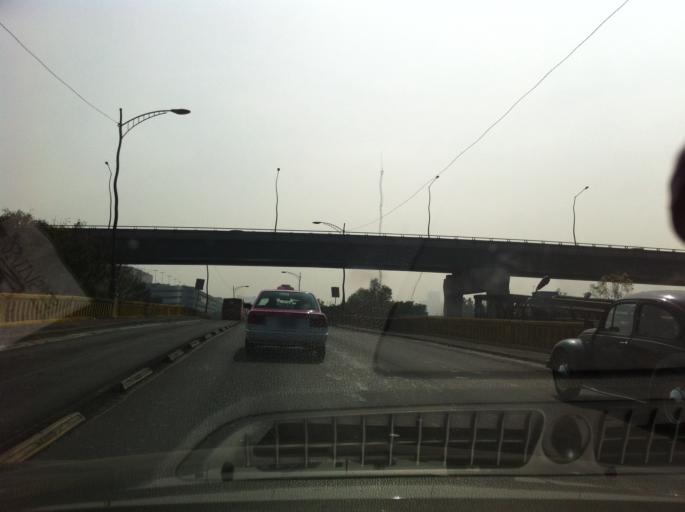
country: MX
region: Mexico City
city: Cuauhtemoc
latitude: 19.4548
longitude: -99.1518
